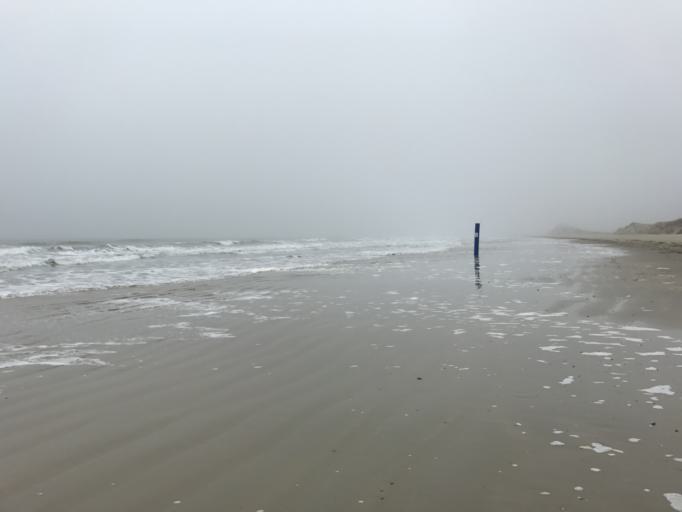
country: DE
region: Lower Saxony
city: Borkum
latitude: 53.6135
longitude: 6.7333
